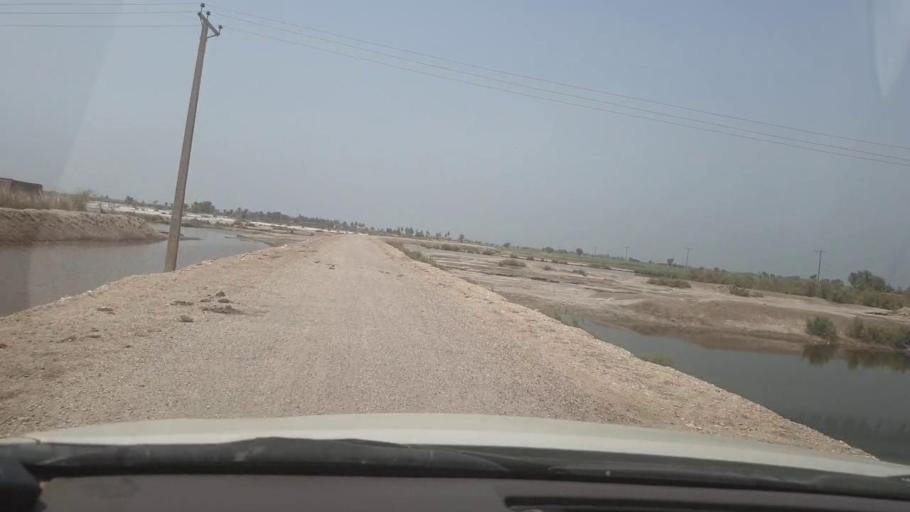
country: PK
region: Sindh
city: Garhi Yasin
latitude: 27.9725
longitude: 68.5492
